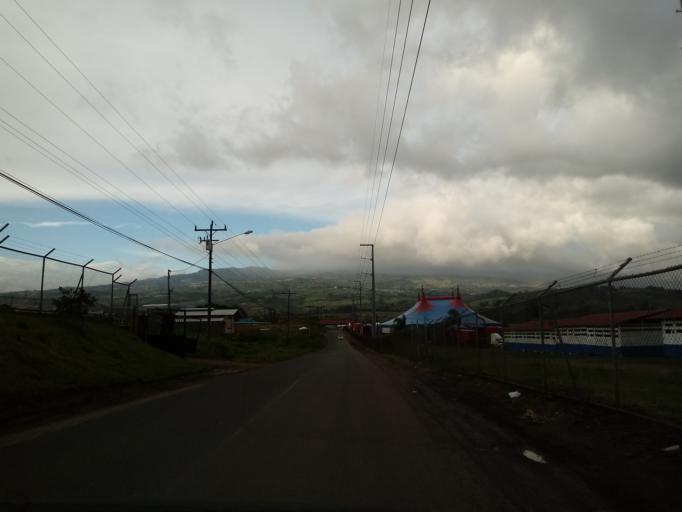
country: CR
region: Cartago
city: Paraiso
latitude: 9.8407
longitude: -83.8863
